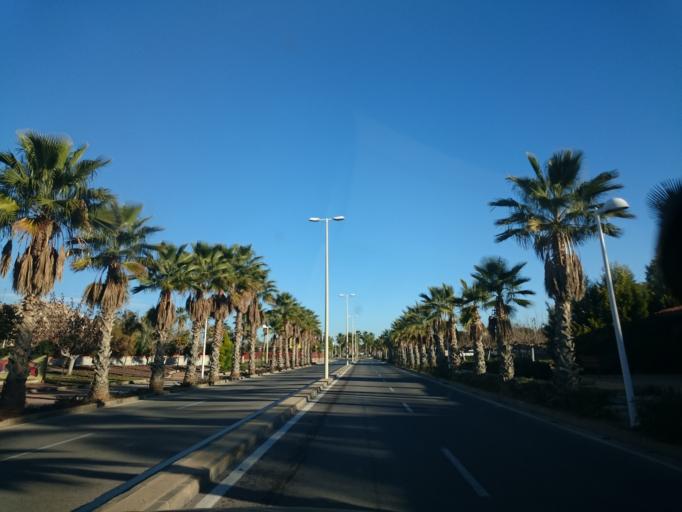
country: ES
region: Valencia
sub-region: Provincia de Castello
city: Orpesa/Oropesa del Mar
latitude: 40.1199
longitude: 0.1555
